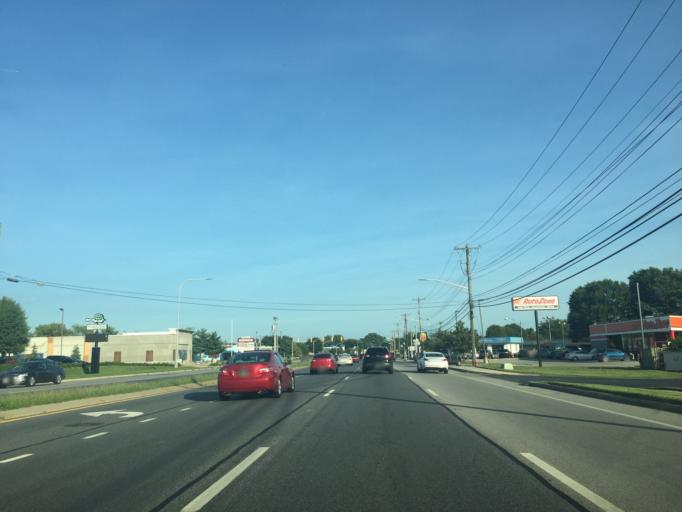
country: US
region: Delaware
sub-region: Kent County
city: Dover
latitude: 39.1730
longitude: -75.5213
